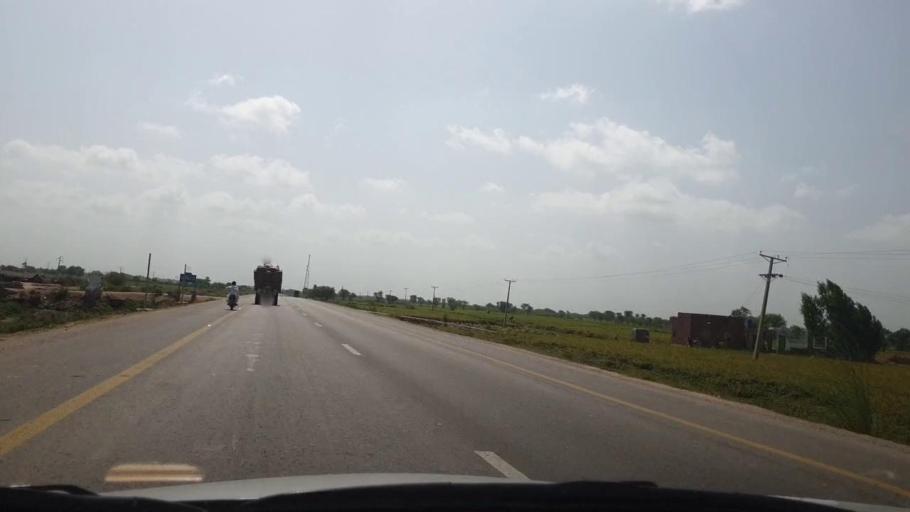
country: PK
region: Sindh
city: Matli
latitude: 24.9605
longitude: 68.6846
